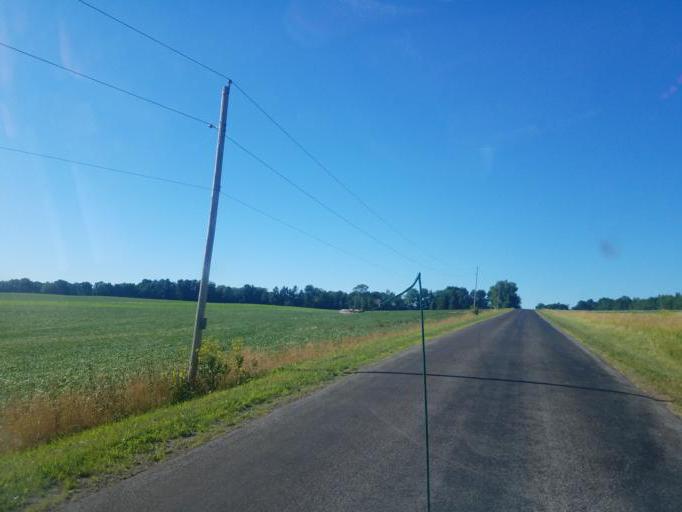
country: US
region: New York
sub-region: Wayne County
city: Lyons
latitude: 43.0944
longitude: -77.0094
